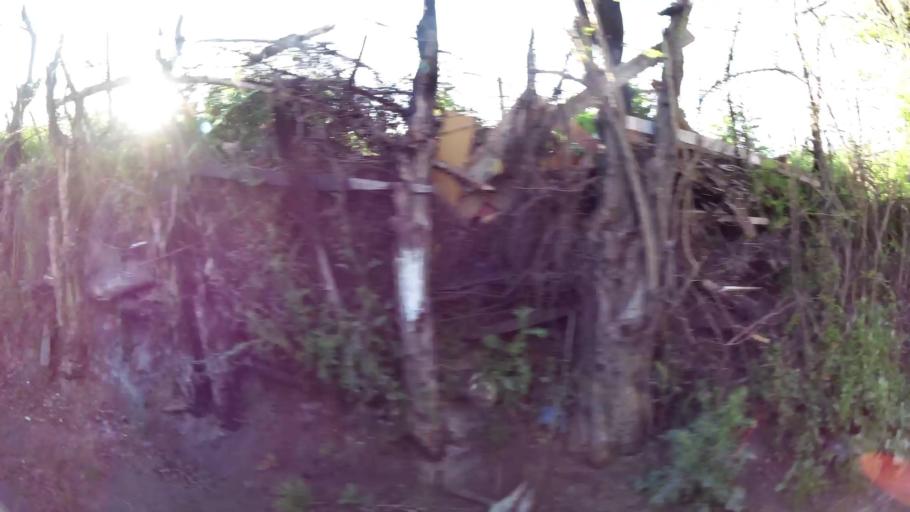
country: CL
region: Santiago Metropolitan
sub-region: Provincia de Santiago
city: Santiago
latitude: -33.3791
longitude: -70.6182
